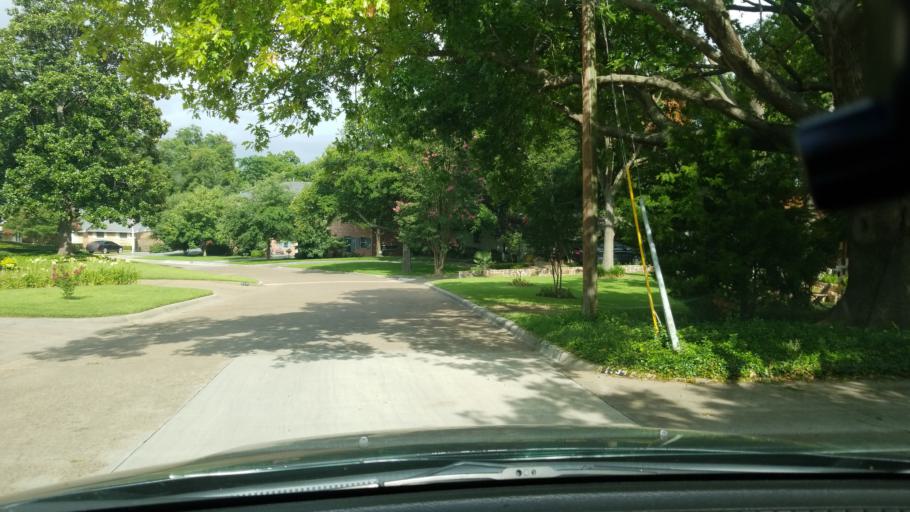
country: US
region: Texas
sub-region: Dallas County
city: Highland Park
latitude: 32.8285
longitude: -96.7134
